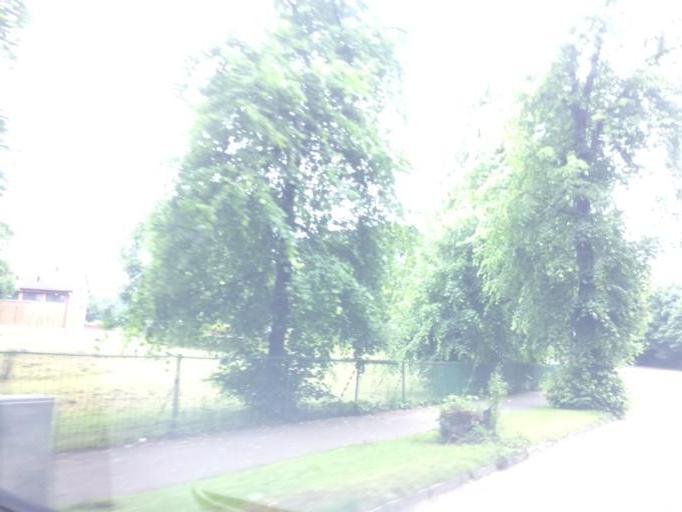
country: GB
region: Scotland
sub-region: East Renfrewshire
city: Giffnock
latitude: 55.8472
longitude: -4.3102
